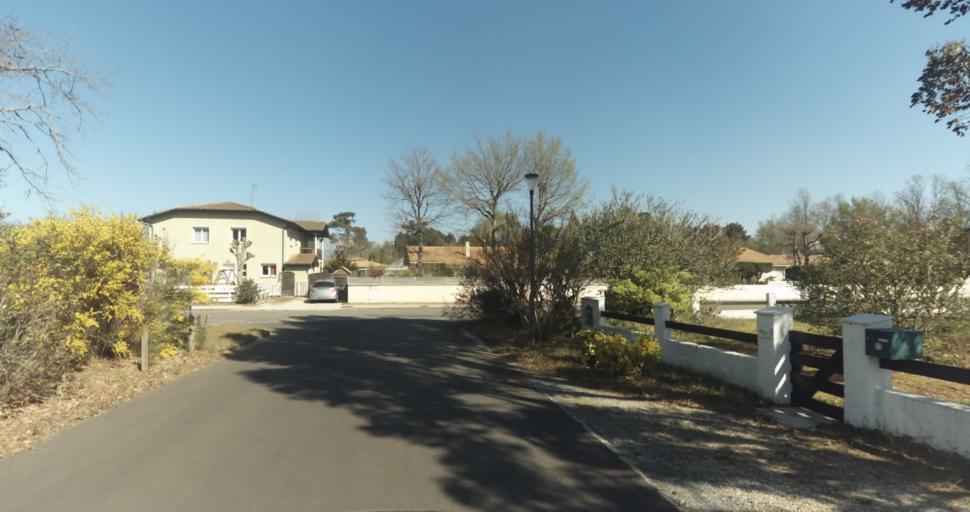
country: FR
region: Aquitaine
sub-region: Departement de la Gironde
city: Martignas-sur-Jalle
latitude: 44.8068
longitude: -0.7809
